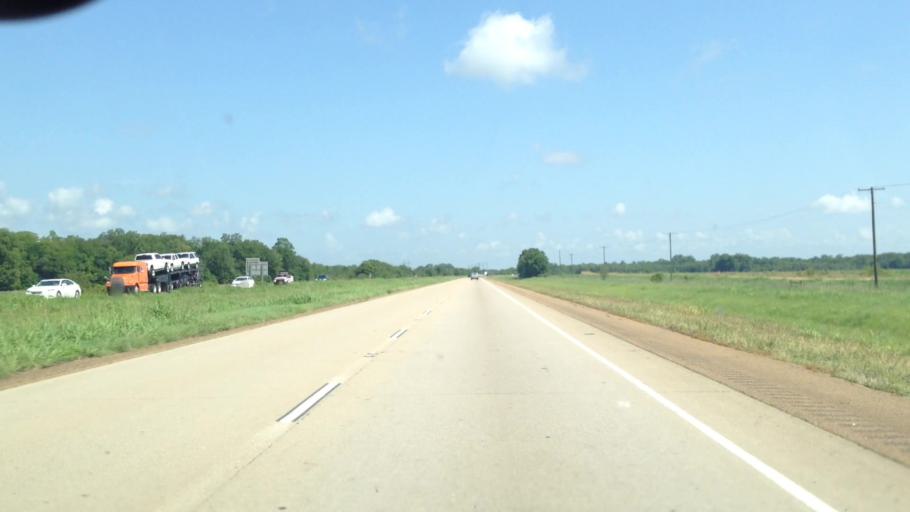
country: US
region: Louisiana
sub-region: Rapides Parish
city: Woodworth
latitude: 31.1805
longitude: -92.4685
